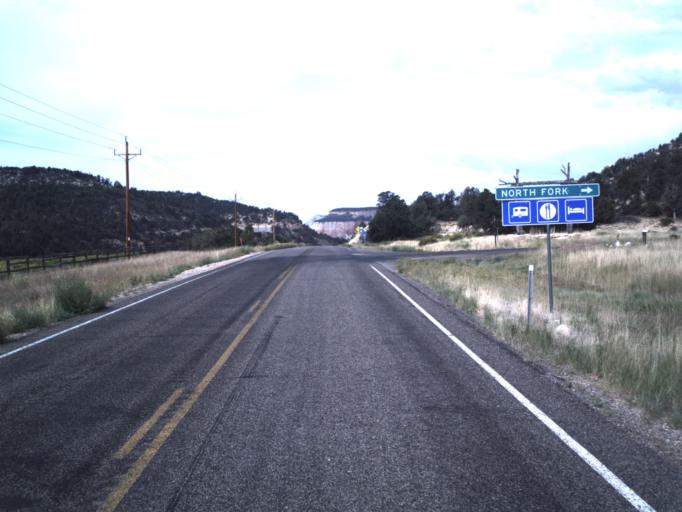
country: US
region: Utah
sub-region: Washington County
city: Hildale
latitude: 37.2393
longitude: -112.8317
